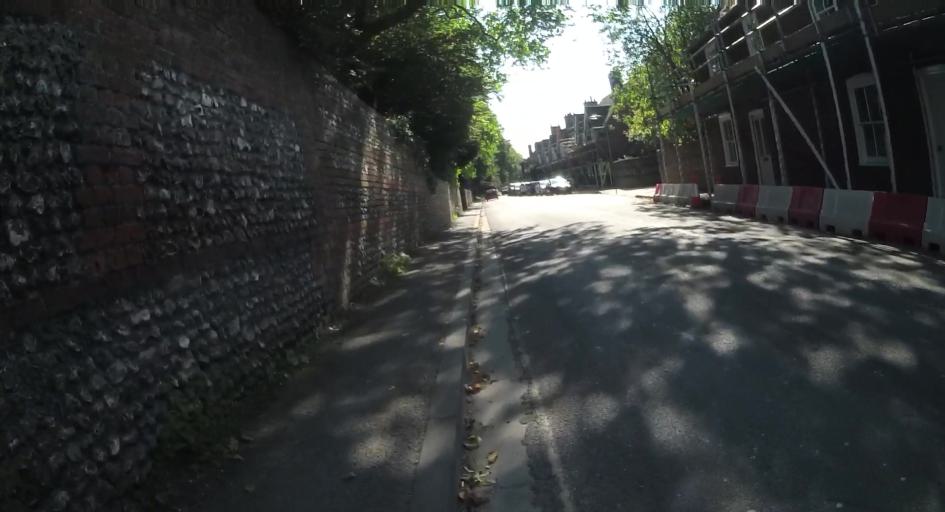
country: GB
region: England
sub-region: Hampshire
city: Winchester
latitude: 51.0554
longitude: -1.3169
